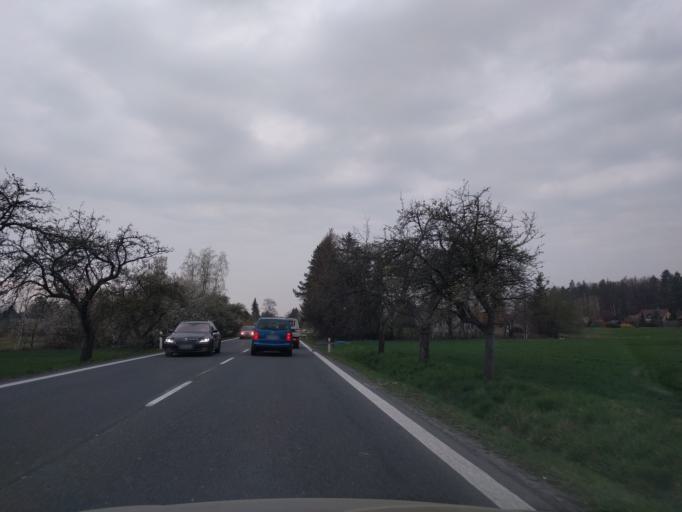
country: CZ
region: Central Bohemia
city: Mukarov
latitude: 49.9893
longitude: 14.7535
